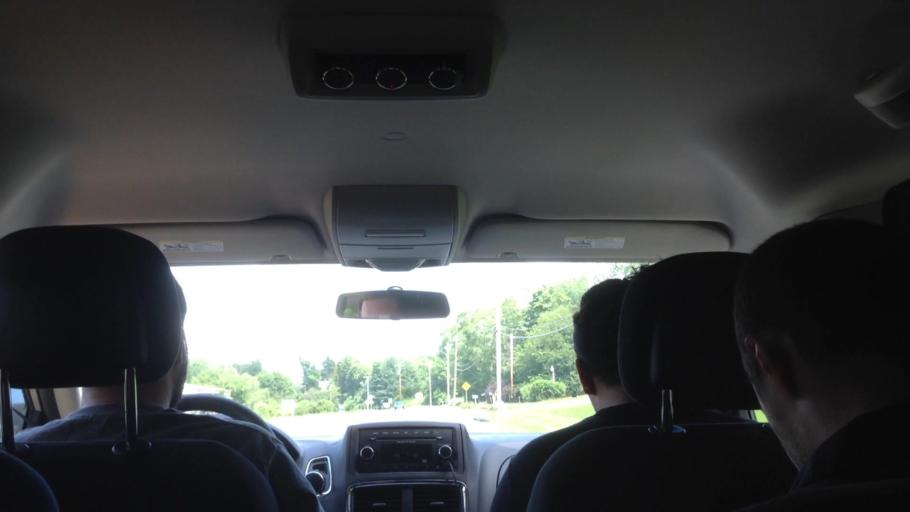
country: US
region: New York
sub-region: Dutchess County
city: Red Hook
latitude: 42.0189
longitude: -73.8513
